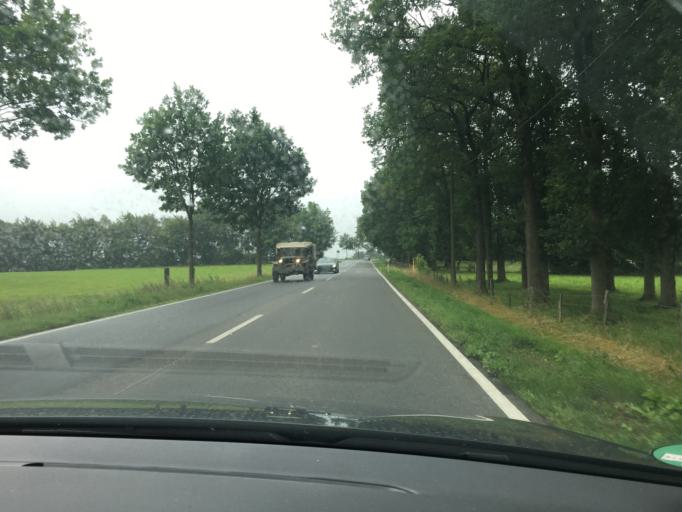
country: DE
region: North Rhine-Westphalia
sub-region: Regierungsbezirk Koln
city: Hurtgenwald
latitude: 50.6749
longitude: 6.3460
